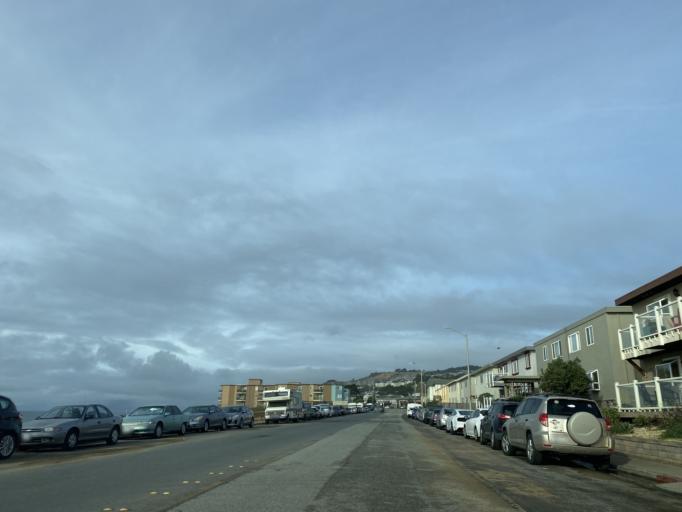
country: US
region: California
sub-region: San Mateo County
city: Pacifica
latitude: 37.6496
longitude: -122.4928
